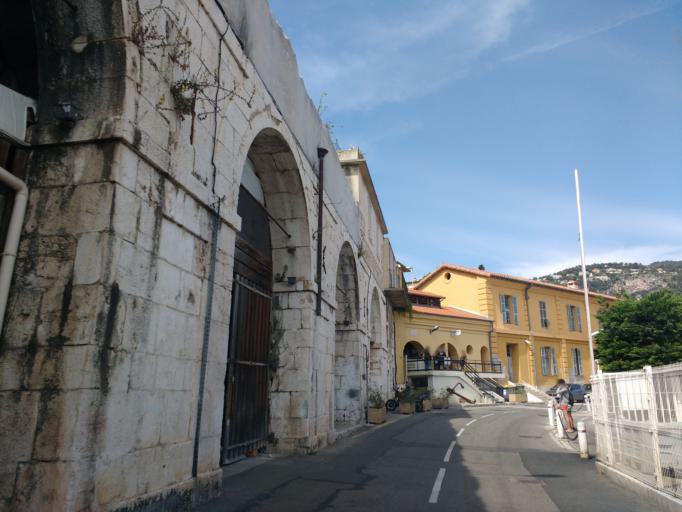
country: FR
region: Provence-Alpes-Cote d'Azur
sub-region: Departement des Alpes-Maritimes
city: Villefranche-sur-Mer
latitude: 43.6982
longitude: 7.3068
